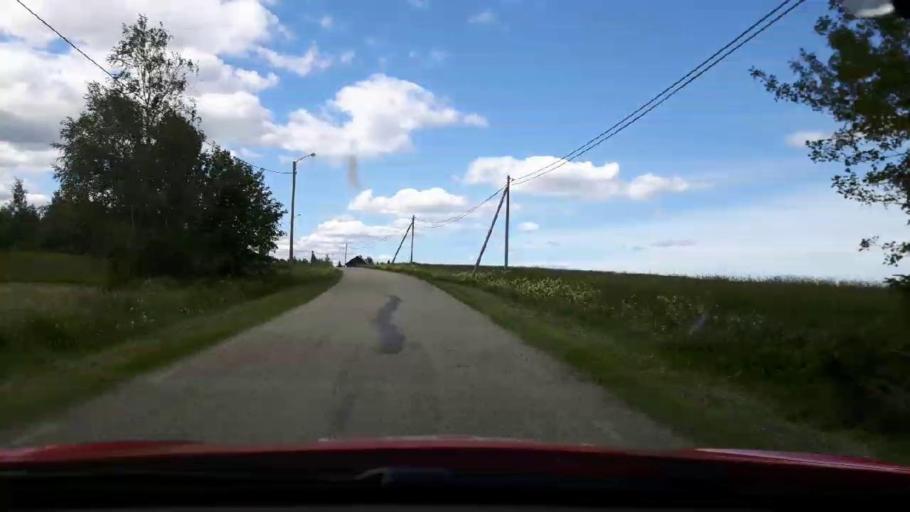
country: SE
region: Jaemtland
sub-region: Bergs Kommun
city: Hoverberg
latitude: 62.8329
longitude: 14.4567
